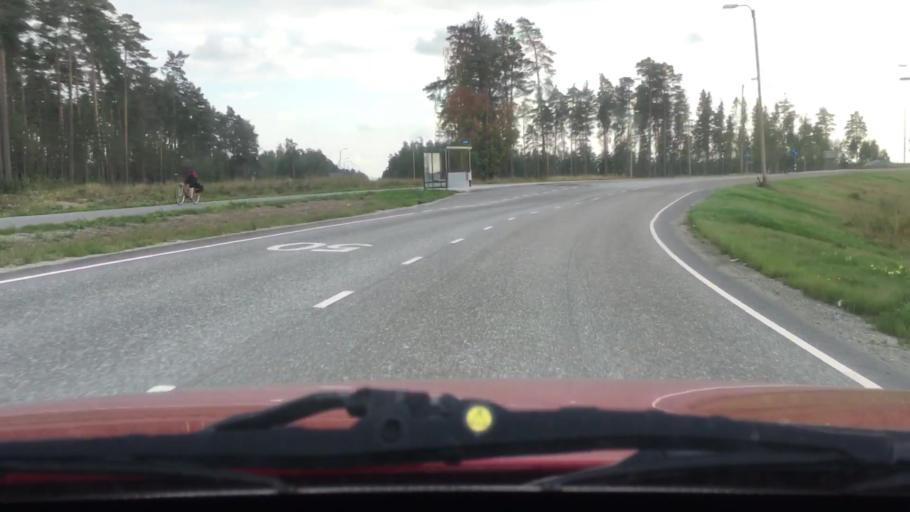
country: FI
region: Varsinais-Suomi
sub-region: Turku
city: Masku
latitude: 60.5436
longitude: 22.1291
